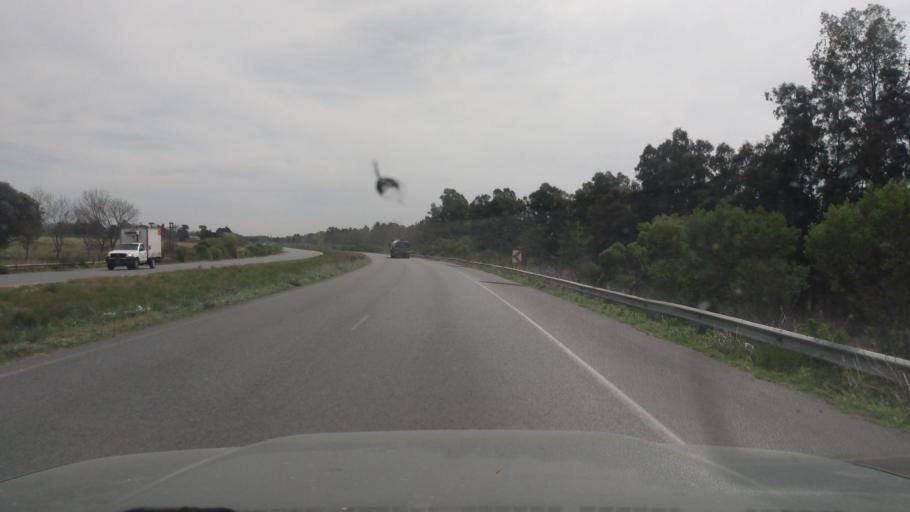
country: AR
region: Buenos Aires
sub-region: Partido de Lujan
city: Lujan
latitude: -34.5168
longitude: -59.0377
